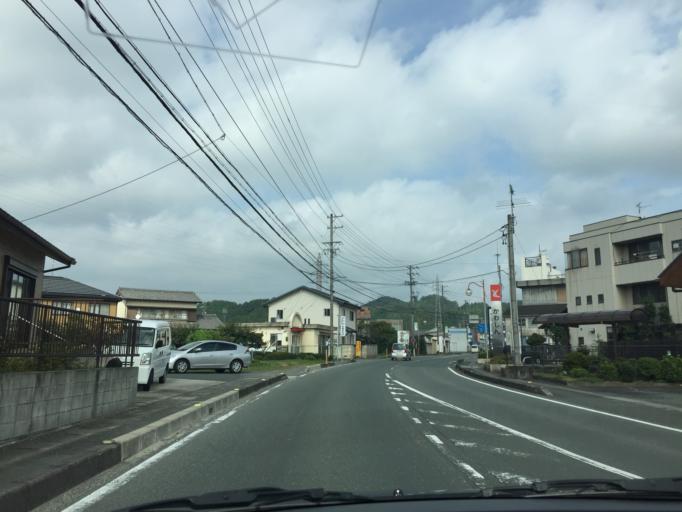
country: JP
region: Aichi
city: Shinshiro
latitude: 34.9332
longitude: 137.5732
